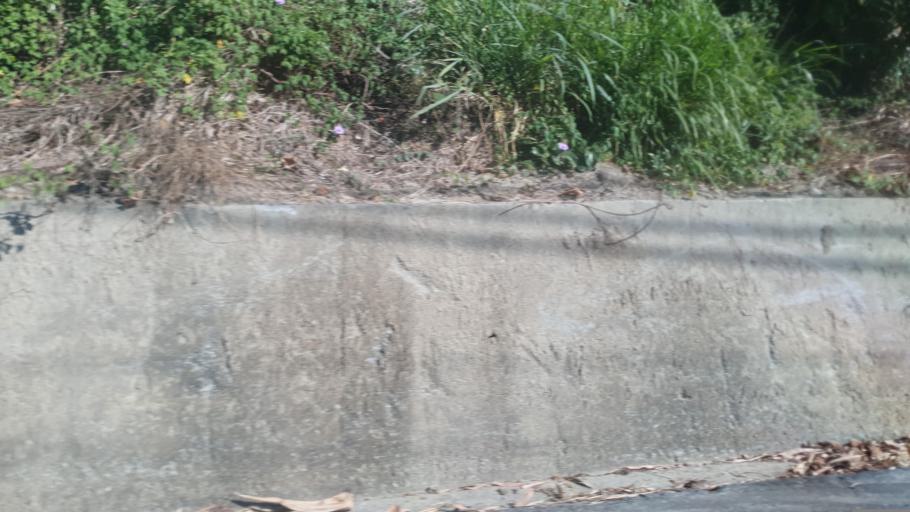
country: TW
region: Taiwan
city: Yujing
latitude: 23.0431
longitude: 120.3969
